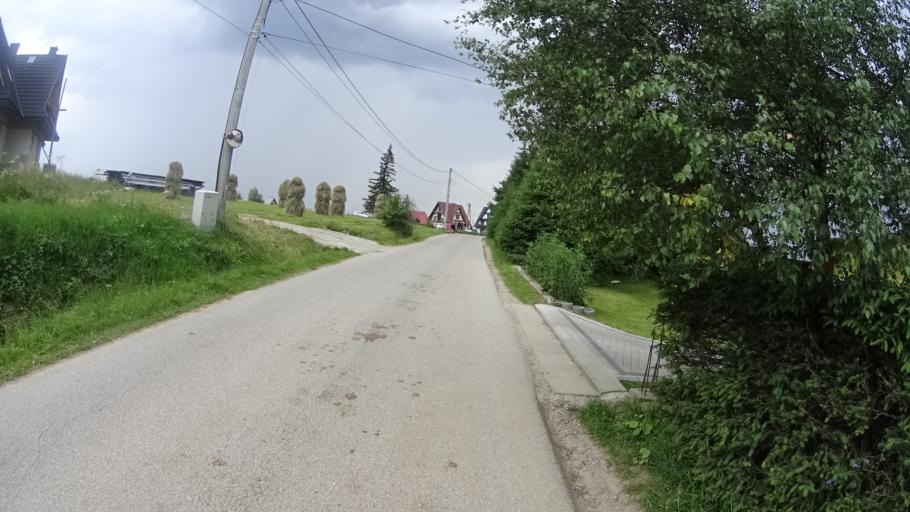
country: PL
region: Lesser Poland Voivodeship
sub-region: Powiat tatrzanski
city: Zakopane
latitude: 49.3225
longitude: 19.9537
